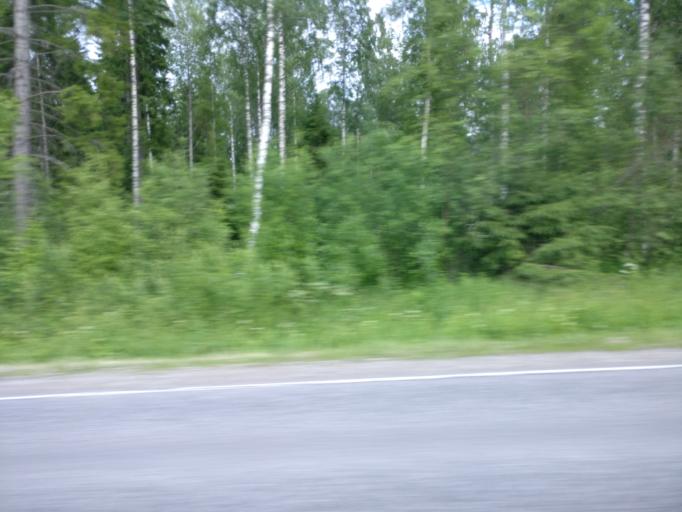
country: FI
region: Southern Savonia
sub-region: Savonlinna
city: Savonlinna
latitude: 61.9556
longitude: 28.9235
